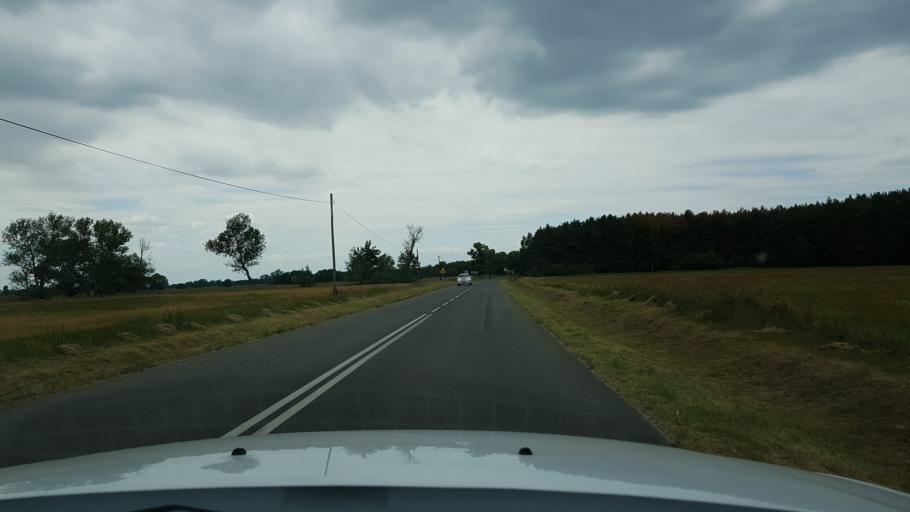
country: DE
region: Brandenburg
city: Manschnow
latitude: 52.6276
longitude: 14.5707
